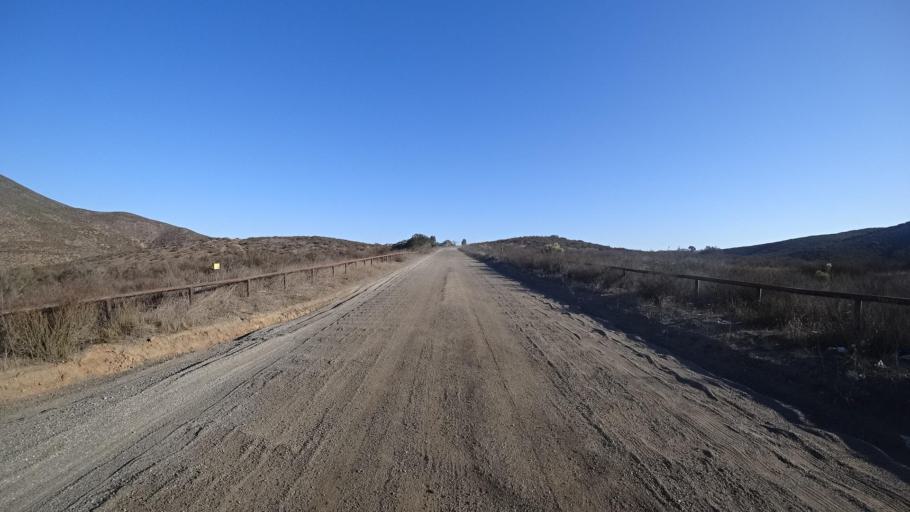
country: US
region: California
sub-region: San Diego County
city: Jamul
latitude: 32.6869
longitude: -116.9103
